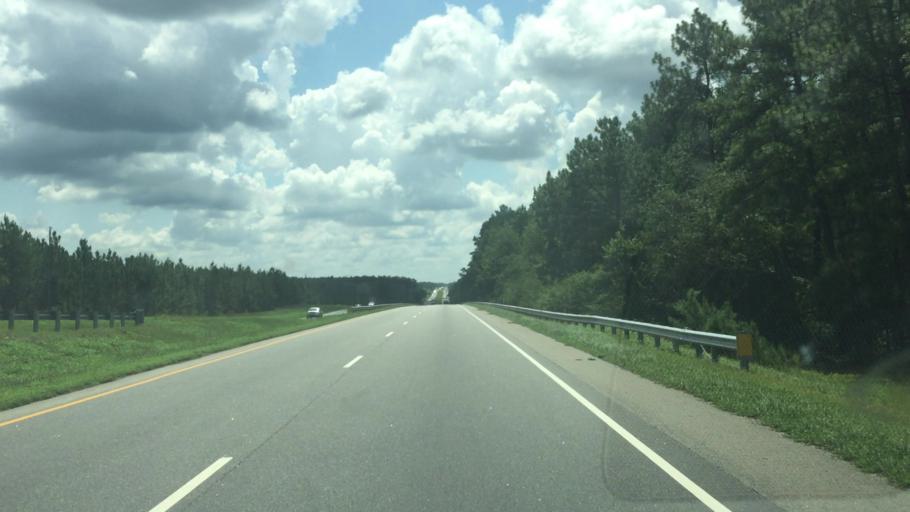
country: US
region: North Carolina
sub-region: Richmond County
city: Hamlet
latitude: 34.8624
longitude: -79.6348
